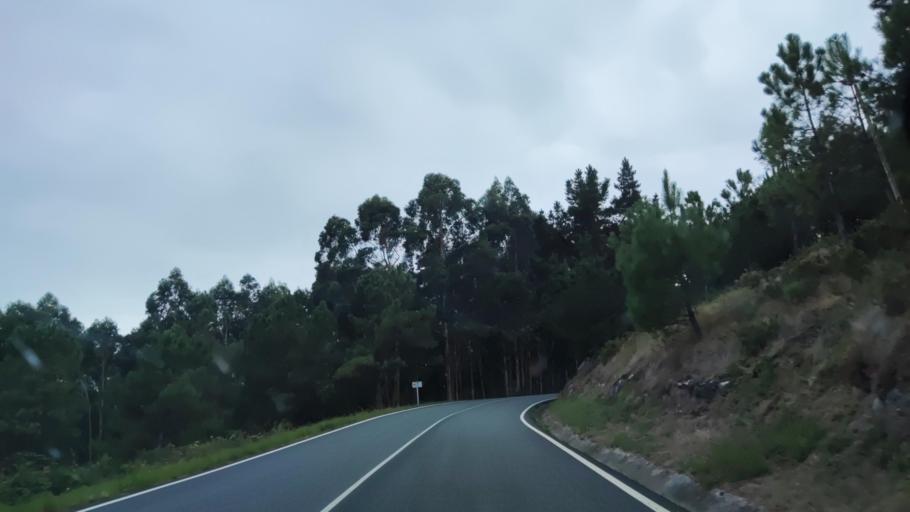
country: ES
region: Galicia
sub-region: Provincia de Pontevedra
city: Catoira
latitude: 42.6618
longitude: -8.7469
